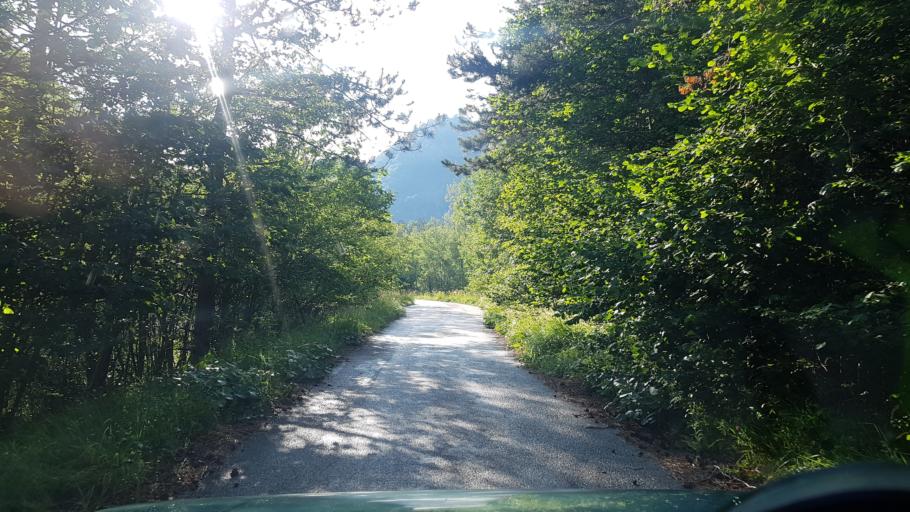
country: IT
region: Friuli Venezia Giulia
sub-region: Provincia di Udine
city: Lusevera
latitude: 46.3104
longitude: 13.2722
